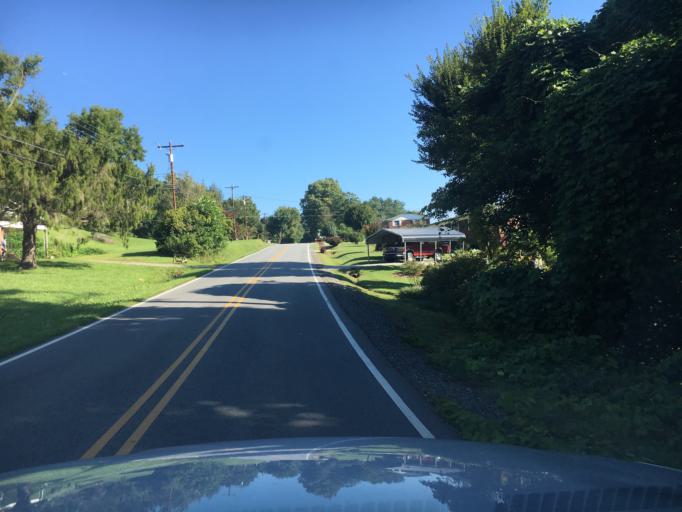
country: US
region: North Carolina
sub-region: McDowell County
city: West Marion
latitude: 35.6603
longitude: -82.0349
